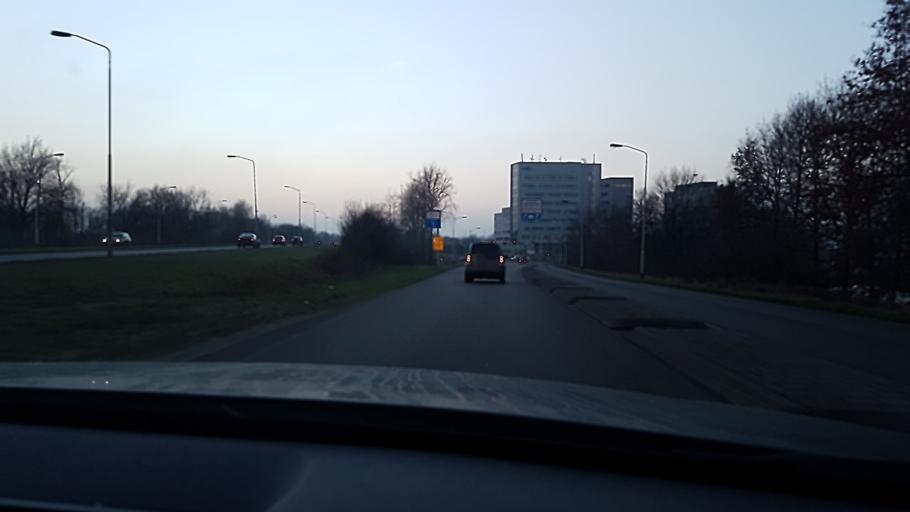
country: NL
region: North Brabant
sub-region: Gemeente Breda
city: Hoge Vucht
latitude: 51.5808
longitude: 4.8085
